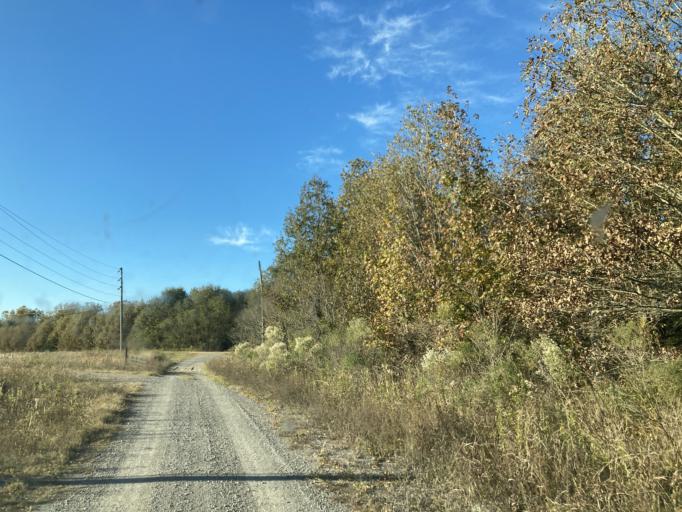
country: US
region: Mississippi
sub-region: Yazoo County
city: Yazoo City
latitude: 32.8955
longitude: -90.4353
